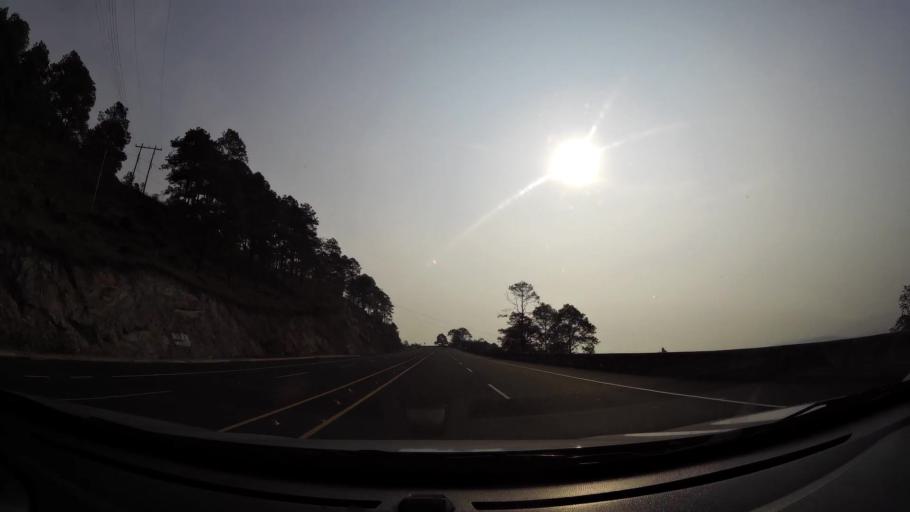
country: HN
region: Francisco Morazan
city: Zambrano
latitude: 14.2444
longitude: -87.3790
